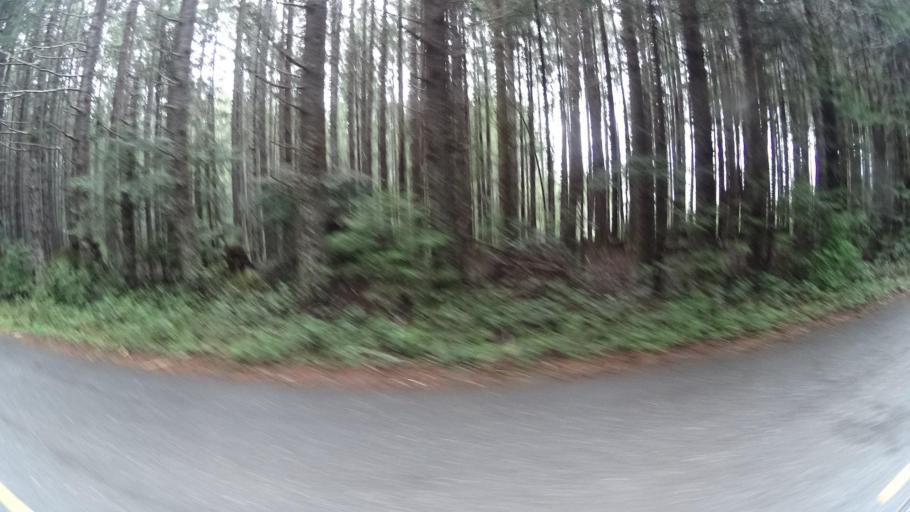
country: US
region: California
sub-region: Humboldt County
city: Westhaven-Moonstone
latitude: 41.2469
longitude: -123.9827
